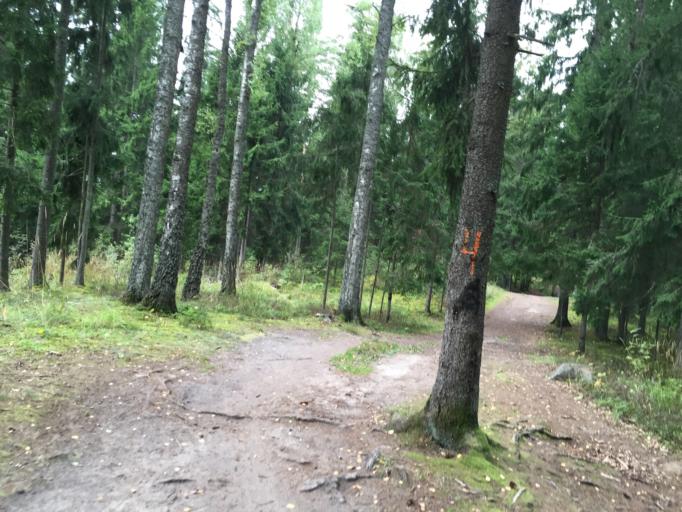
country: LV
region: Ogre
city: Ogre
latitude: 56.8325
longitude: 24.5791
